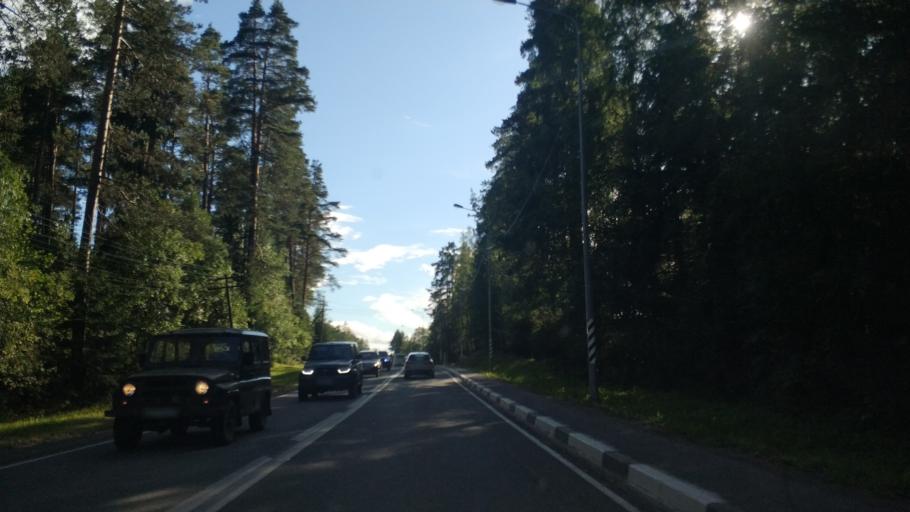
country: RU
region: Republic of Karelia
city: Lakhdenpokh'ya
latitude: 61.5320
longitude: 30.2083
